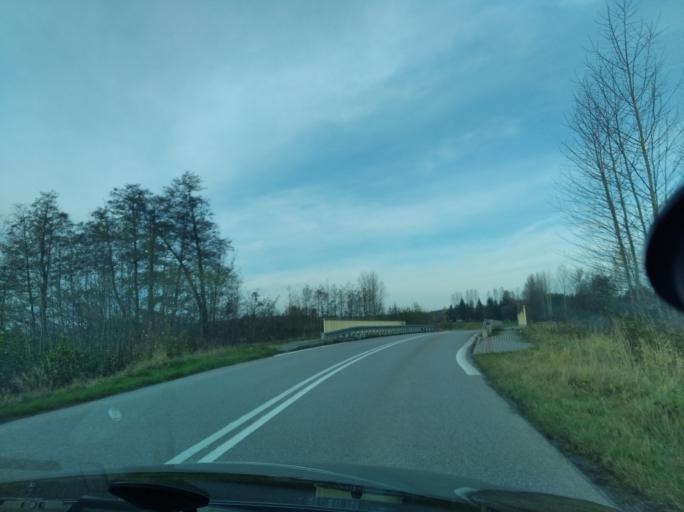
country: PL
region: Subcarpathian Voivodeship
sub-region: Powiat lancucki
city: Albigowa
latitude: 50.0356
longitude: 22.2205
